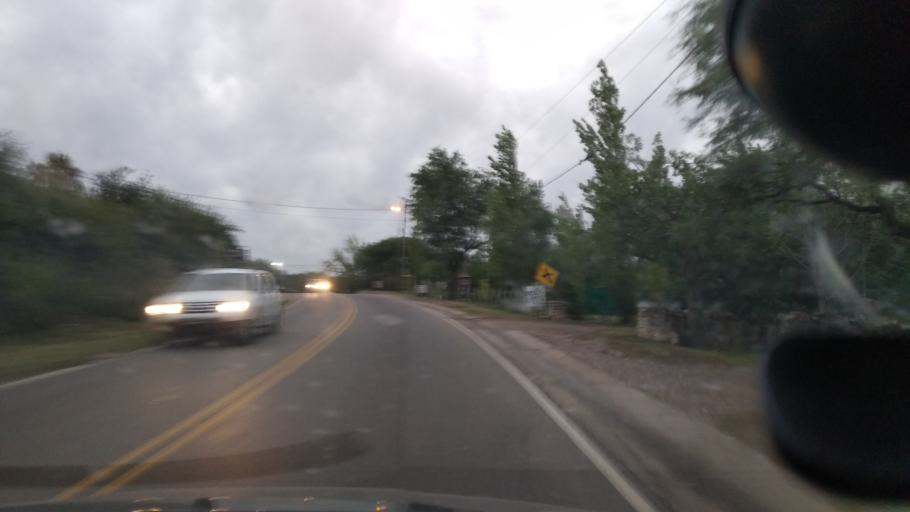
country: AR
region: Cordoba
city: Villa Las Rosas
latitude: -31.9232
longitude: -65.0399
